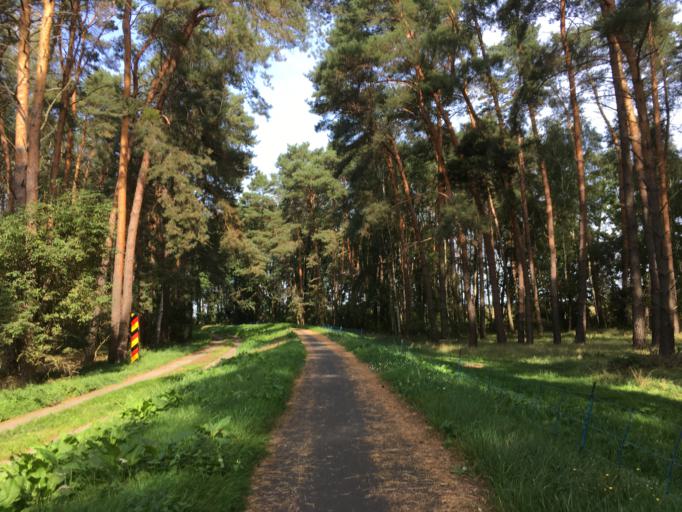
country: PL
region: Lubusz
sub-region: Powiat krosnienski
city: Gubin
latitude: 52.0236
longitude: 14.7394
